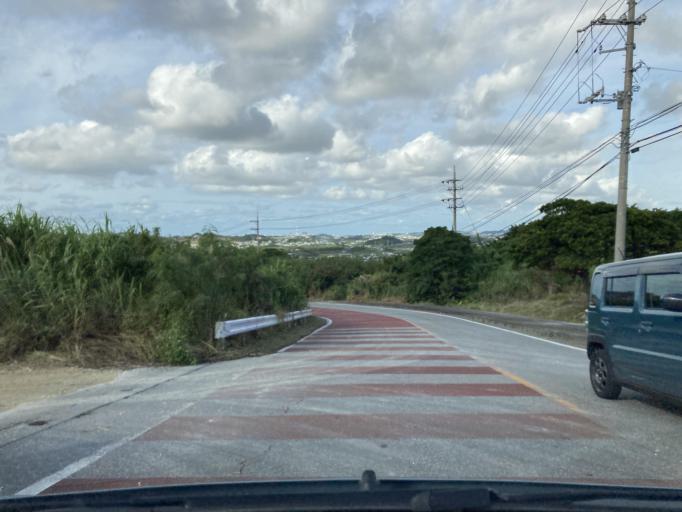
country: JP
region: Okinawa
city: Itoman
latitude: 26.1289
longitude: 127.7129
